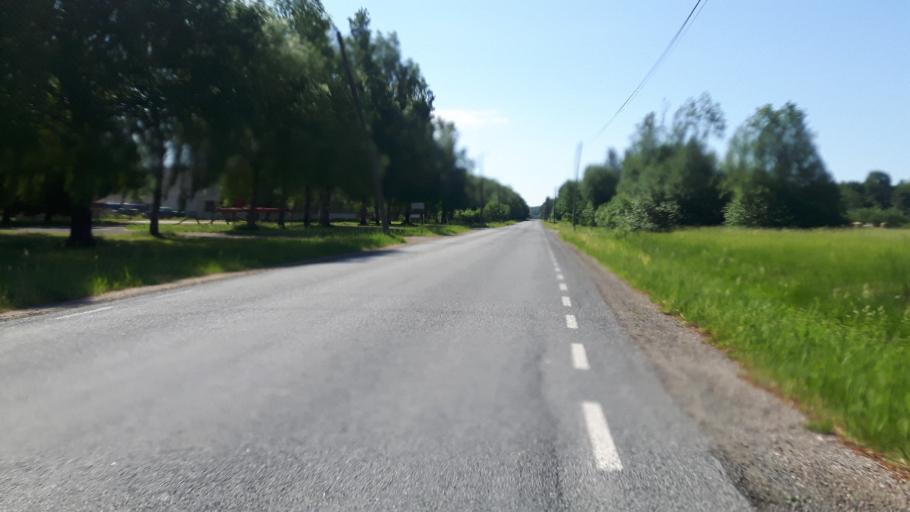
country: EE
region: Paernumaa
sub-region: Vaendra vald (alev)
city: Vandra
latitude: 58.6438
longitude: 25.0276
